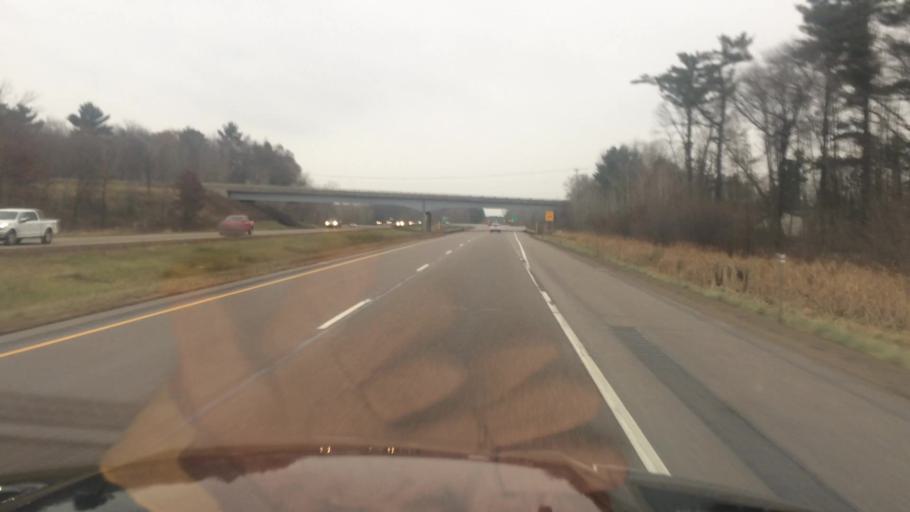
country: US
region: Wisconsin
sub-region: Portage County
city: Stevens Point
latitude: 44.5539
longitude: -89.5852
